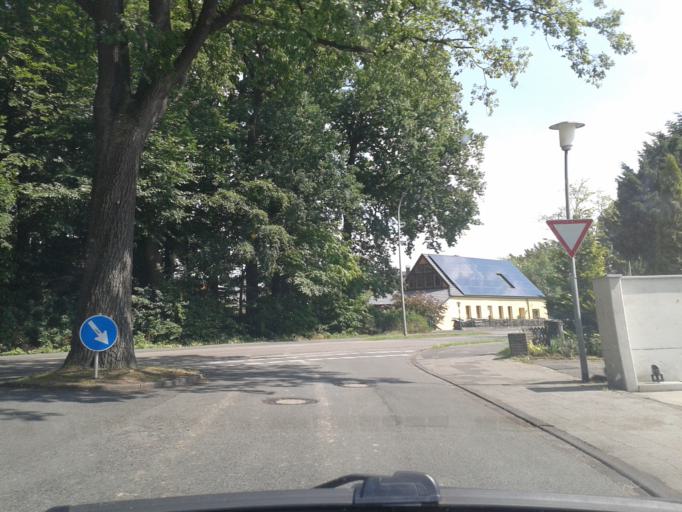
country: DE
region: North Rhine-Westphalia
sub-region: Regierungsbezirk Detmold
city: Paderborn
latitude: 51.7317
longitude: 8.7407
